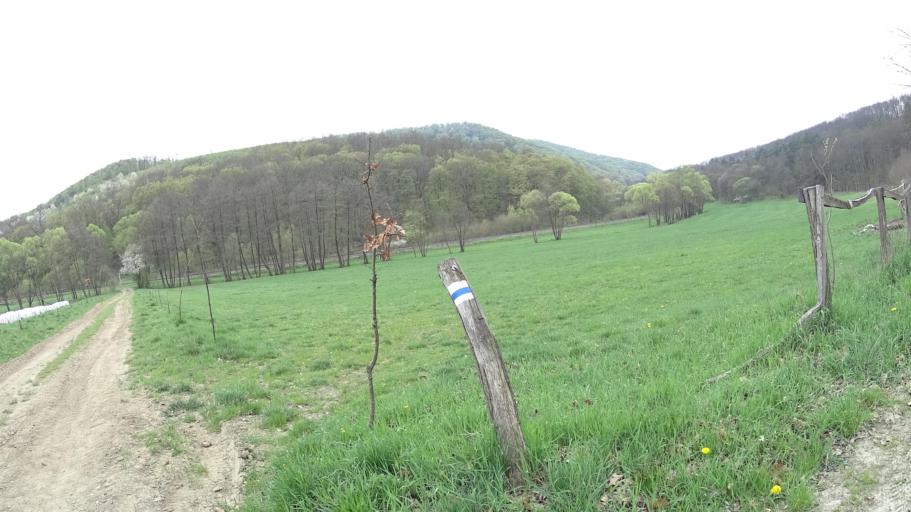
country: HU
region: Nograd
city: Diosjeno
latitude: 47.8891
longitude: 19.0511
